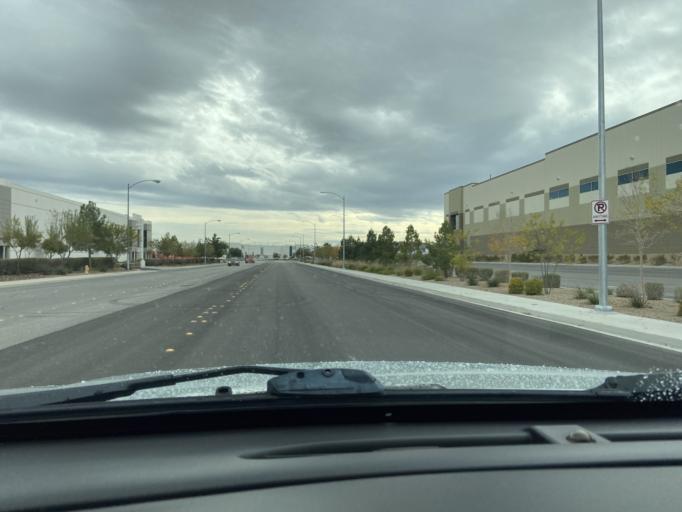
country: US
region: Nevada
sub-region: Clark County
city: North Las Vegas
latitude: 36.2451
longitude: -115.1079
